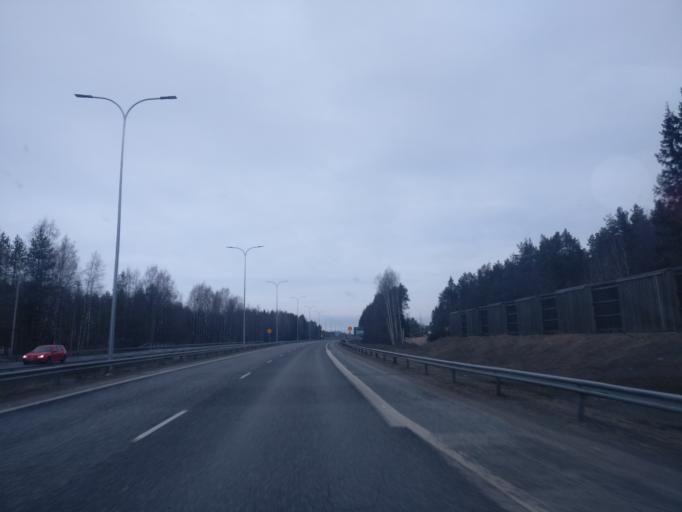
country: FI
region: Northern Ostrobothnia
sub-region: Oulu
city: Oulu
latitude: 65.0430
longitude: 25.4696
